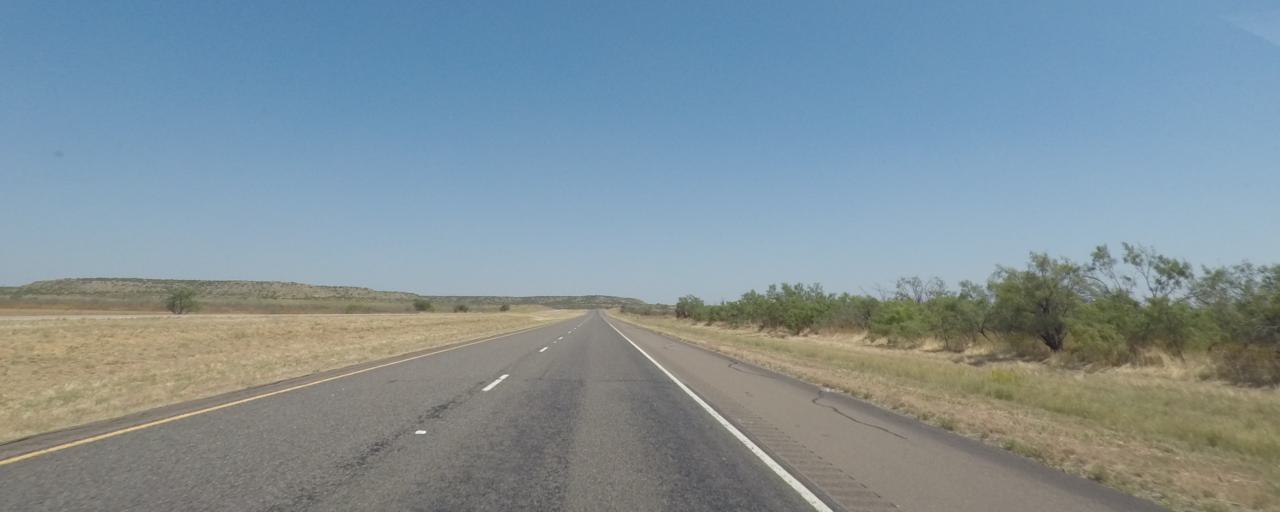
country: US
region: Texas
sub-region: Dickens County
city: Dickens
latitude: 33.6358
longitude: -100.8942
